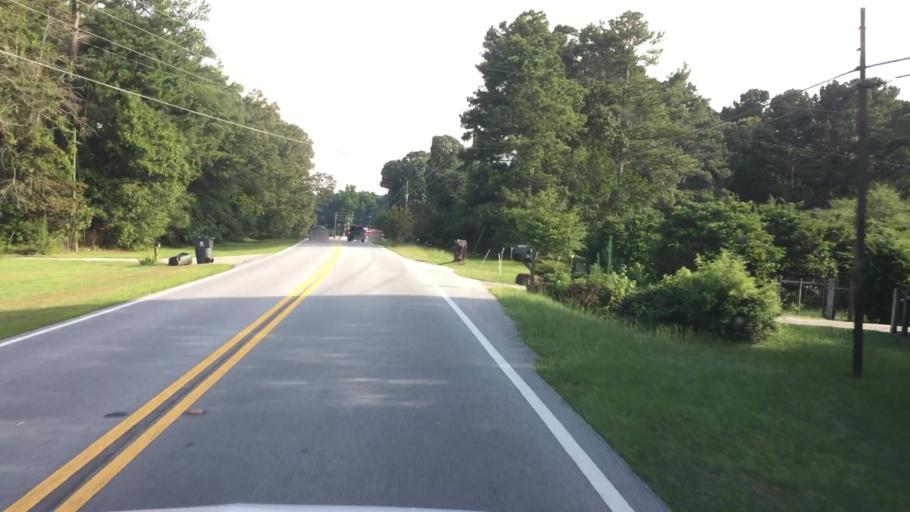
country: US
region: Georgia
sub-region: DeKalb County
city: Pine Mountain
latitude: 33.6114
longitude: -84.1369
